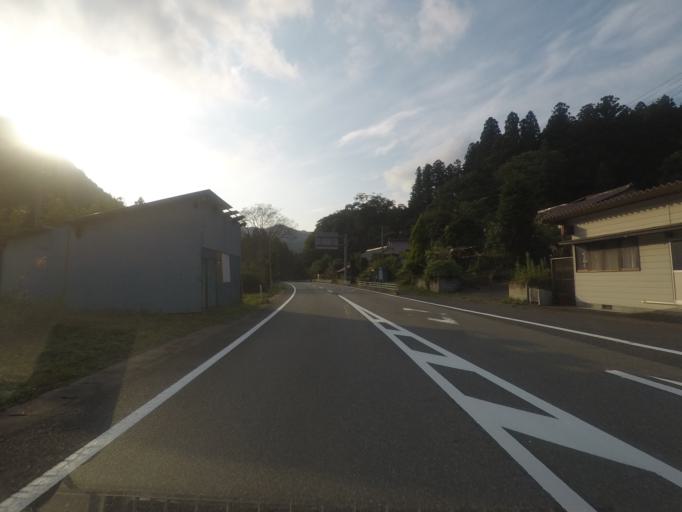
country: JP
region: Fukushima
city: Namie
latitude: 37.5419
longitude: 140.8612
